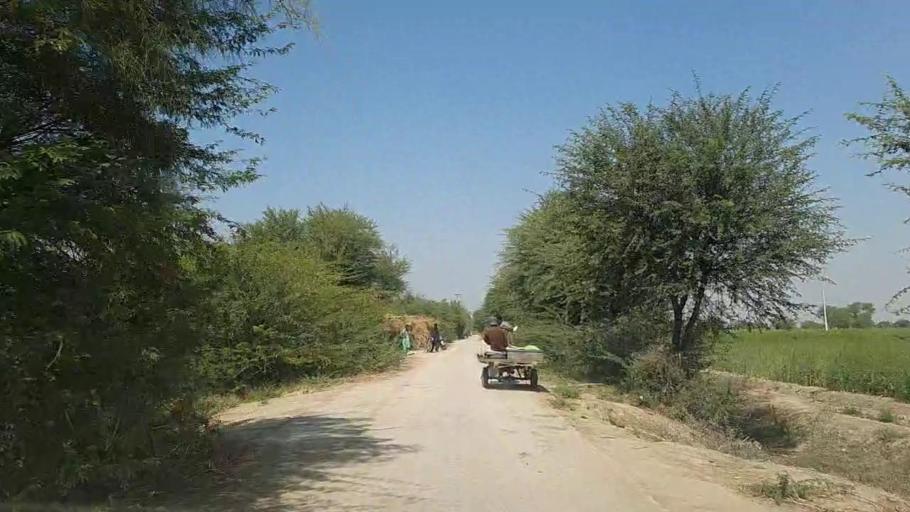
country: PK
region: Sindh
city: Naukot
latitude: 24.8741
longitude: 69.3844
